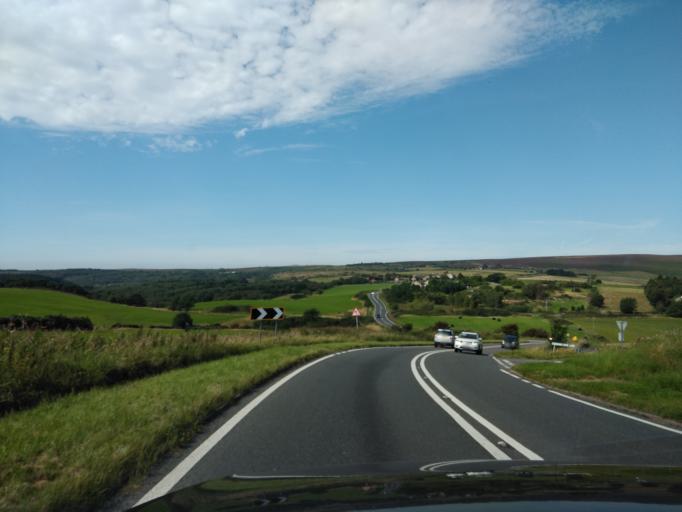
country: GB
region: England
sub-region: Derbyshire
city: Dronfield
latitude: 53.2954
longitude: -1.5399
